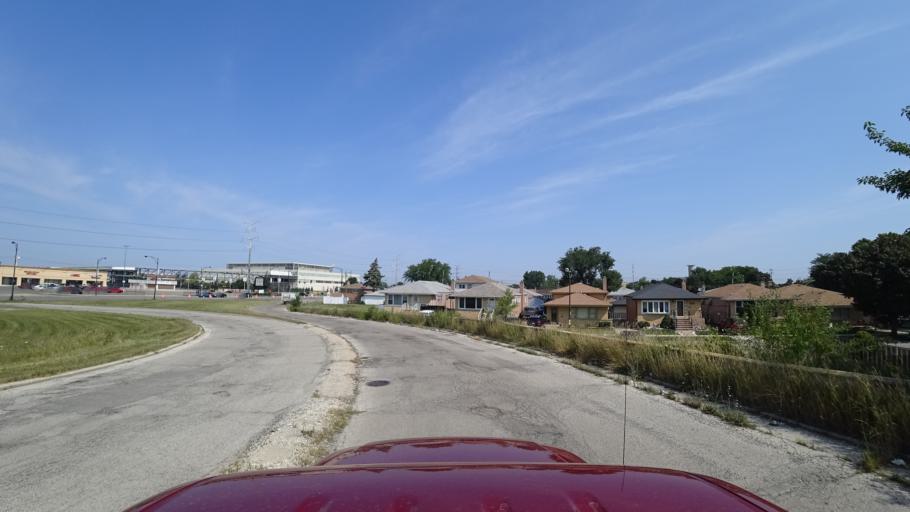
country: US
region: Illinois
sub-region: Cook County
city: Hometown
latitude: 41.7538
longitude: -87.7209
